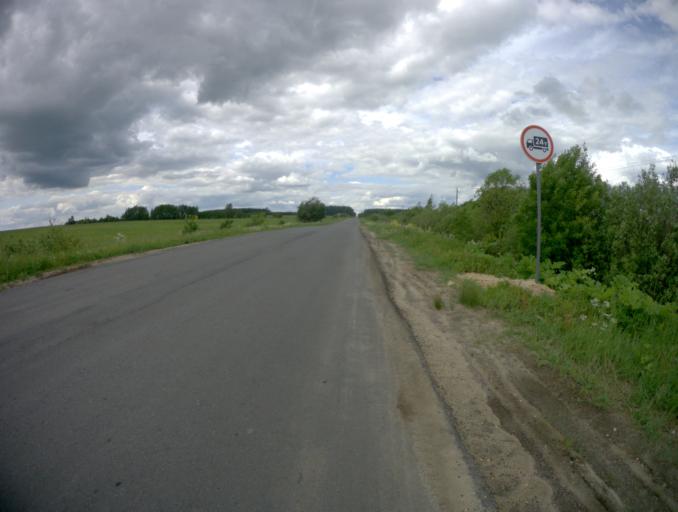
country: RU
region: Vladimir
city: Stavrovo
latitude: 56.2755
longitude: 39.8135
